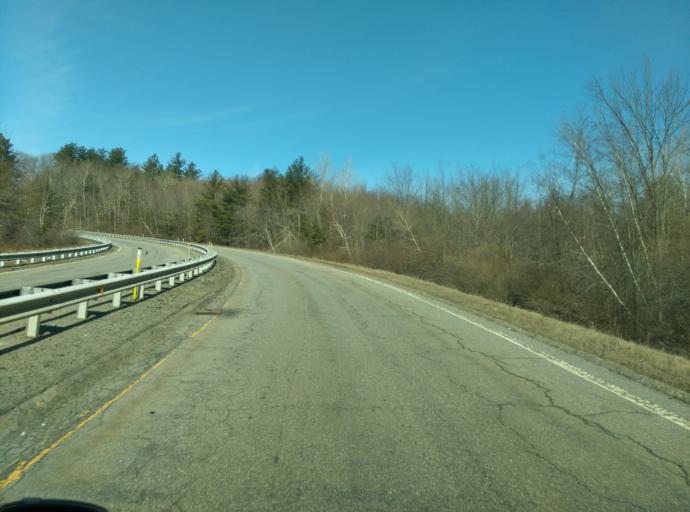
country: US
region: Massachusetts
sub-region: Essex County
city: Lawrence
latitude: 42.7487
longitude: -71.1548
